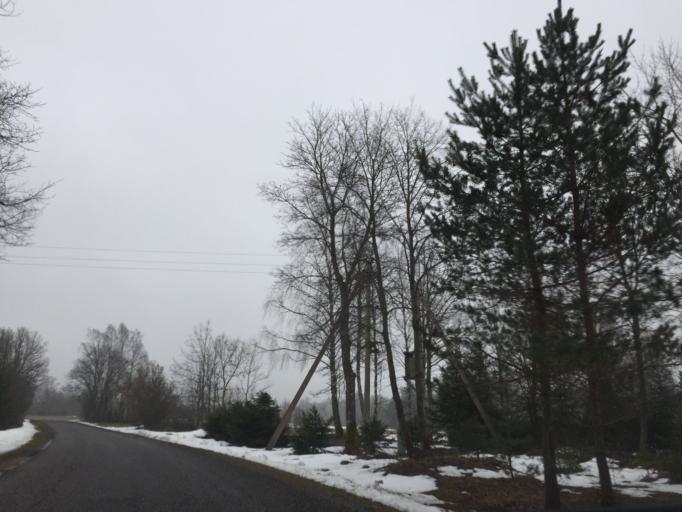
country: EE
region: Saare
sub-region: Kuressaare linn
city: Kuressaare
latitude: 58.2749
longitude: 22.5716
